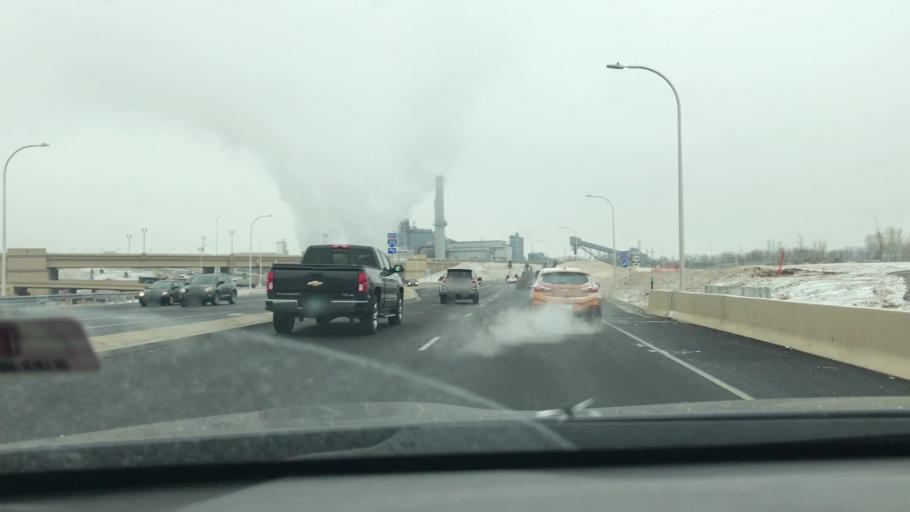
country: US
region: Colorado
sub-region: El Paso County
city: Colorado Springs
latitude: 38.8296
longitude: -104.8381
